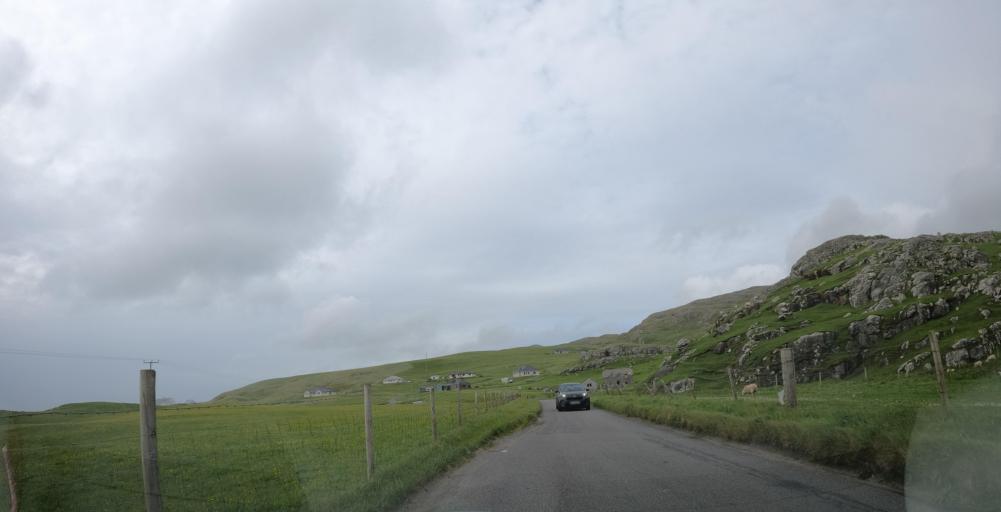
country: GB
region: Scotland
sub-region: Eilean Siar
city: Barra
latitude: 56.9715
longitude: -7.5154
